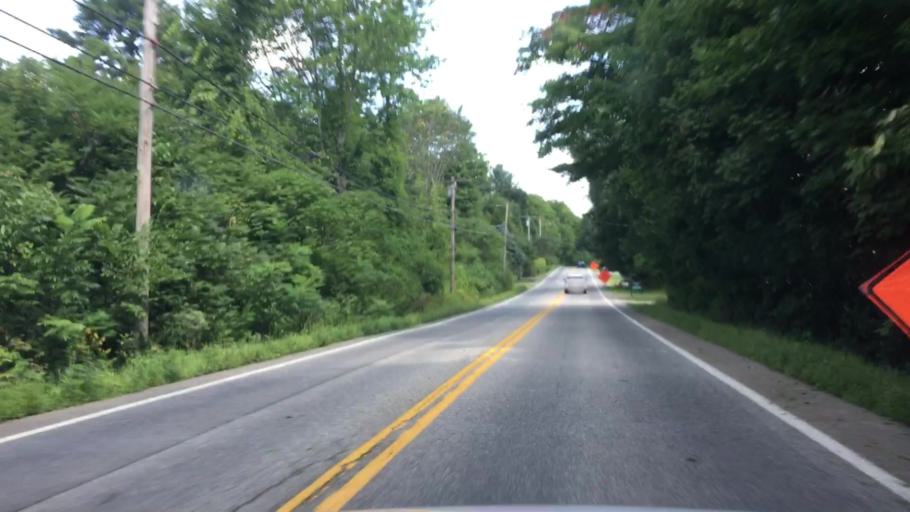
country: US
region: Maine
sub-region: Kennebec County
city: Augusta
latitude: 44.3319
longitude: -69.8168
